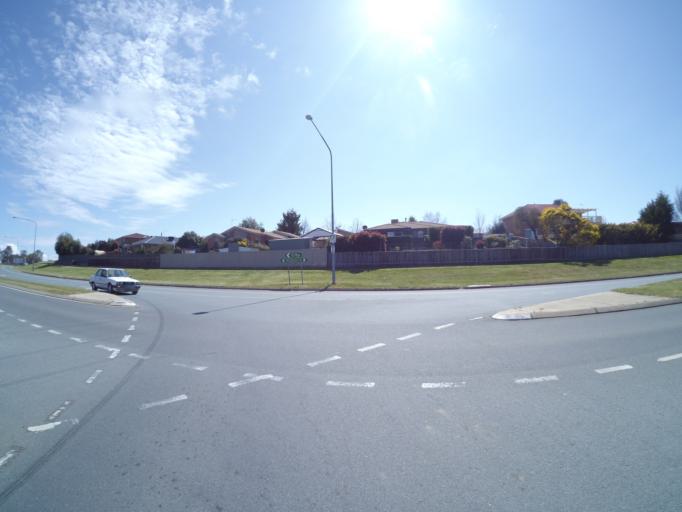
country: AU
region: Australian Capital Territory
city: Macarthur
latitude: -35.4501
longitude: 149.0812
